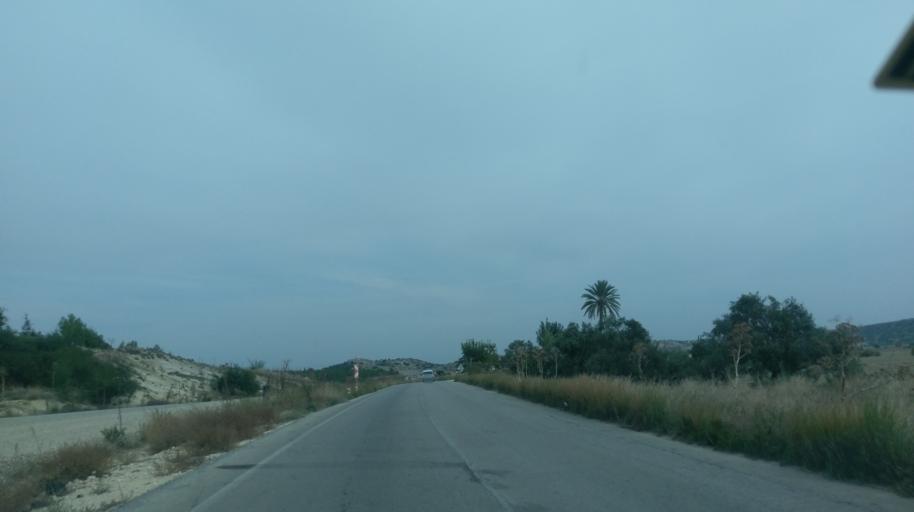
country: CY
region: Ammochostos
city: Trikomo
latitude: 35.3356
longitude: 33.9798
